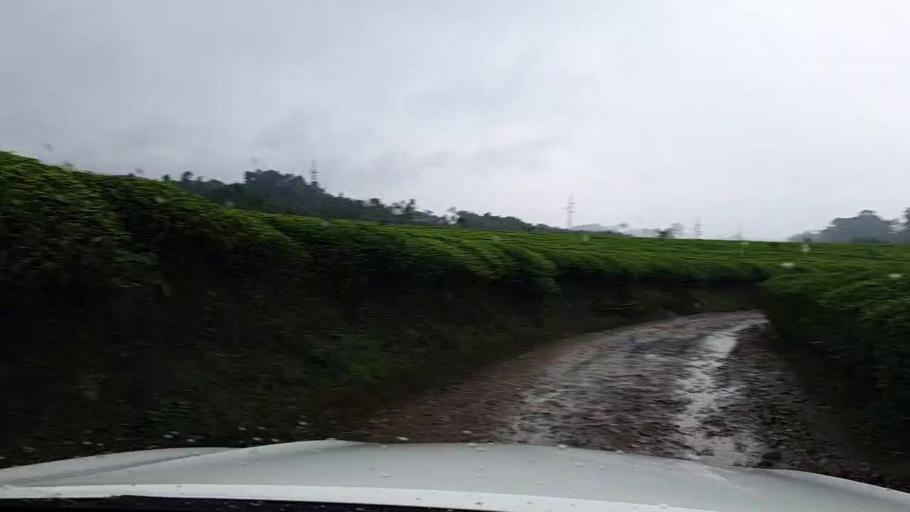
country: RW
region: Western Province
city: Cyangugu
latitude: -2.4553
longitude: 29.0394
